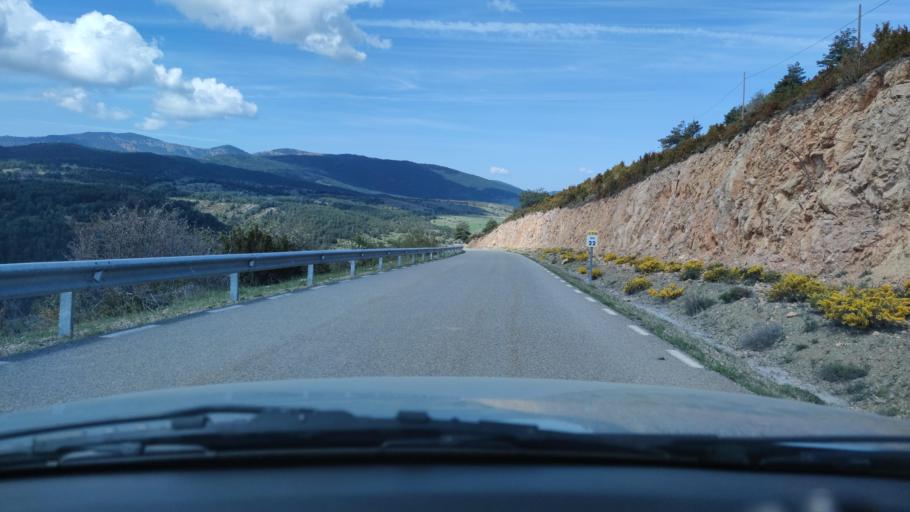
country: ES
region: Catalonia
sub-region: Provincia de Lleida
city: Coll de Nargo
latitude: 42.2820
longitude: 1.2300
